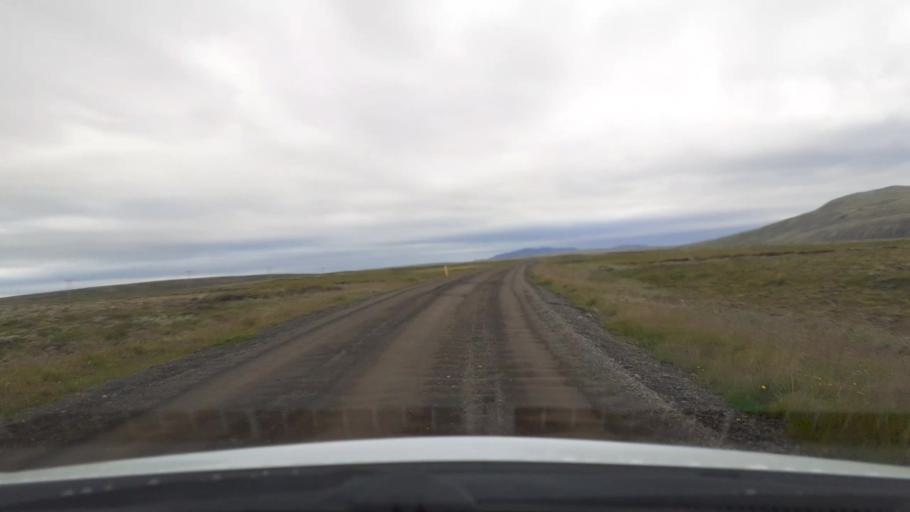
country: IS
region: Capital Region
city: Mosfellsbaer
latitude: 64.1960
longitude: -21.5485
